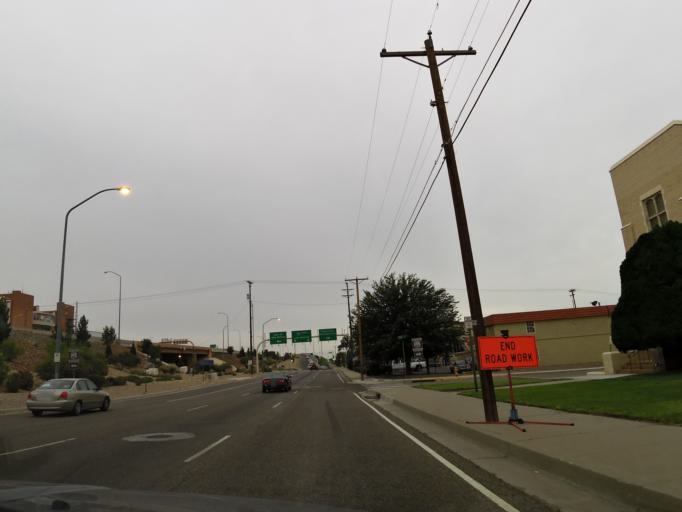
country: US
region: New Mexico
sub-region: Bernalillo County
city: Albuquerque
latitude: 35.0841
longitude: -106.6371
